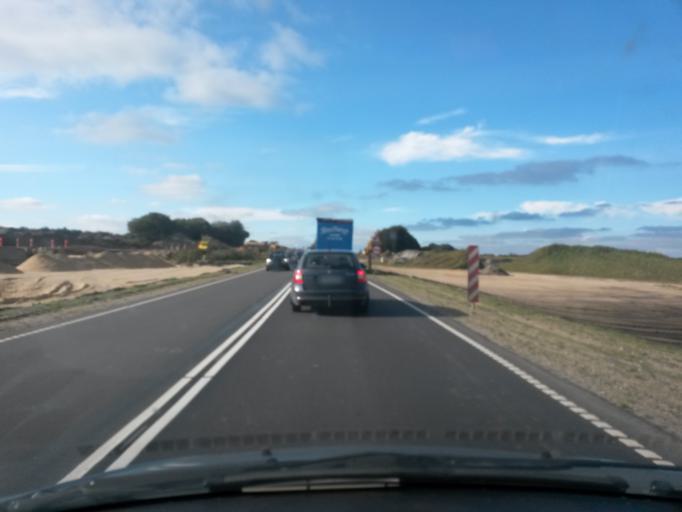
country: DK
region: Central Jutland
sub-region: Herning Kommune
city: Avlum
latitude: 56.2937
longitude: 8.7295
